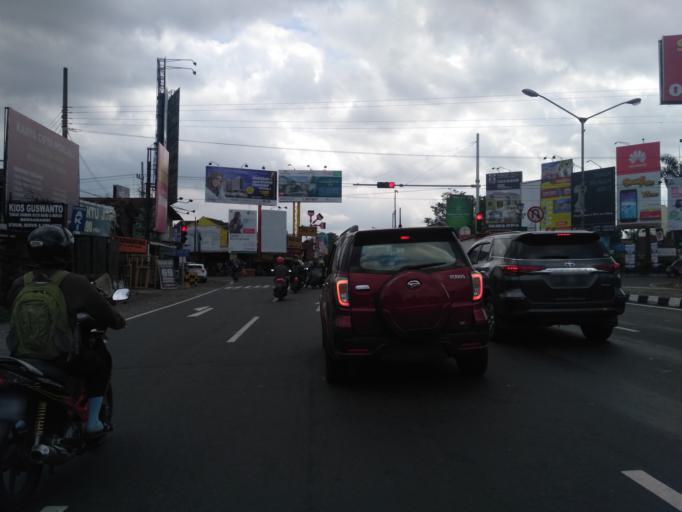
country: ID
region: Daerah Istimewa Yogyakarta
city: Melati
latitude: -7.7514
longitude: 110.3718
